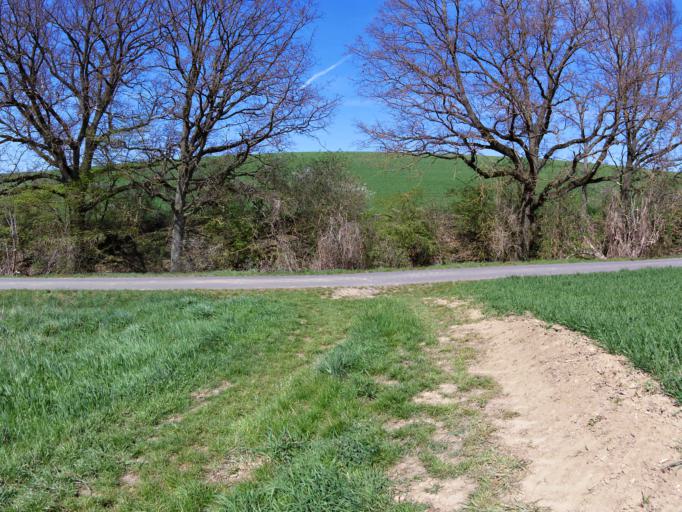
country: DE
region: Bavaria
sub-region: Regierungsbezirk Unterfranken
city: Rottendorf
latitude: 49.7983
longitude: 10.0446
